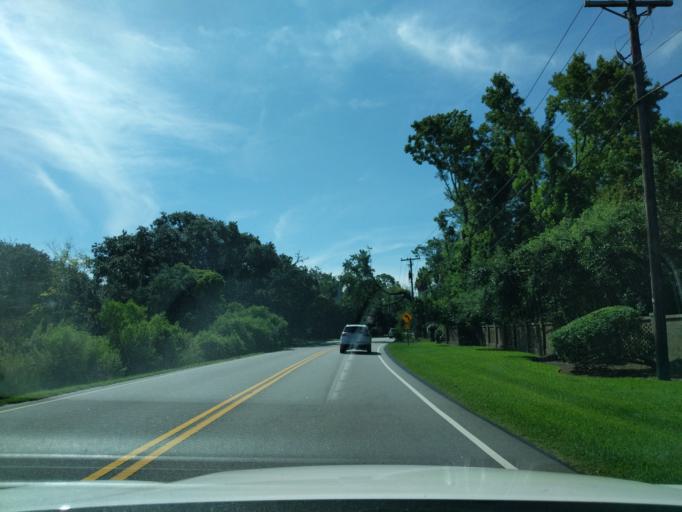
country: US
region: South Carolina
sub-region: Charleston County
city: Charleston
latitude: 32.7531
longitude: -79.9540
